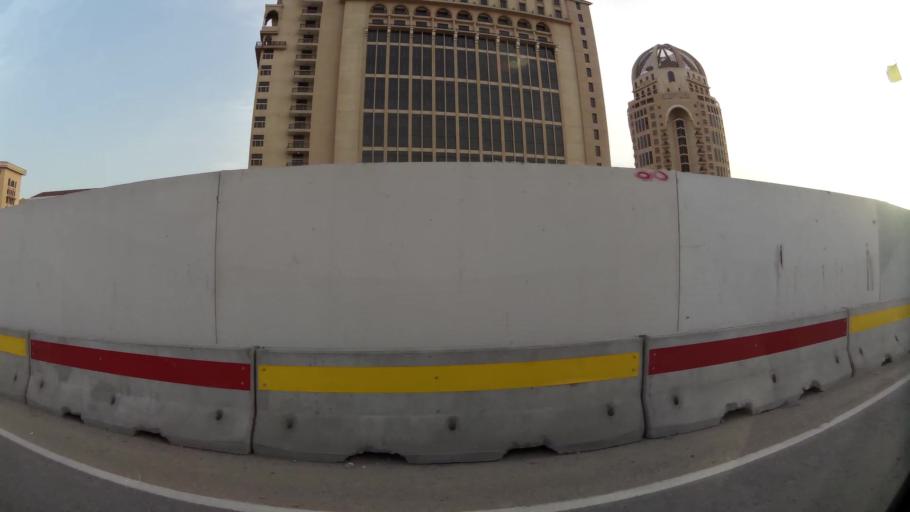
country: QA
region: Baladiyat ad Dawhah
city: Doha
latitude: 25.3515
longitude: 51.5282
